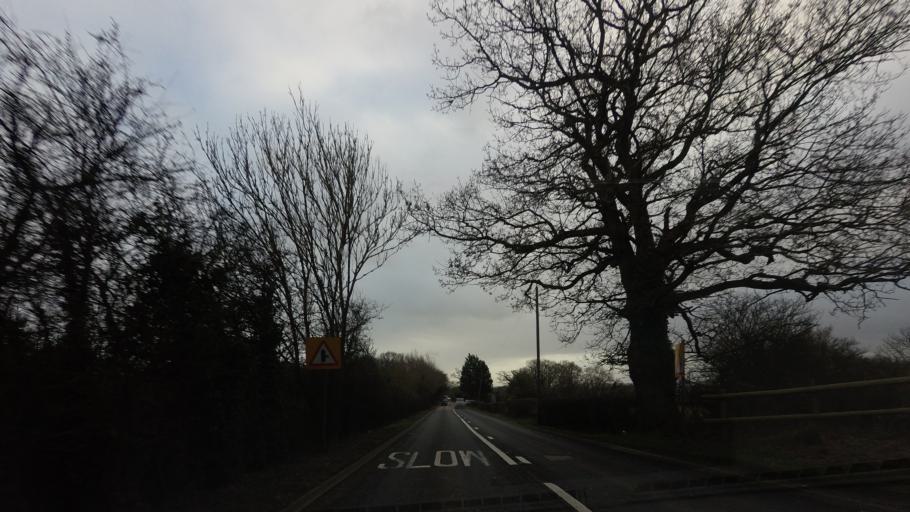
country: GB
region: England
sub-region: Kent
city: East Peckham
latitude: 51.2347
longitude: 0.3831
